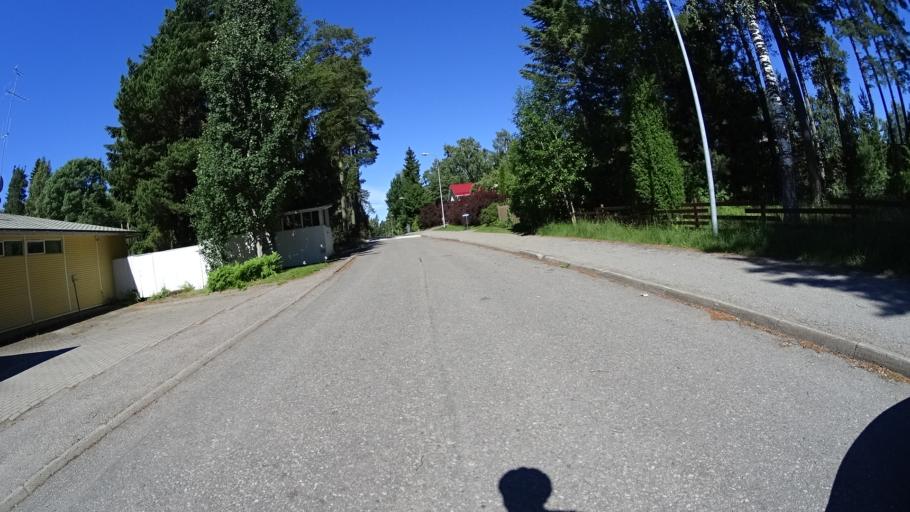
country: FI
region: Uusimaa
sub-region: Helsinki
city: Koukkuniemi
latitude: 60.1565
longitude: 24.7598
